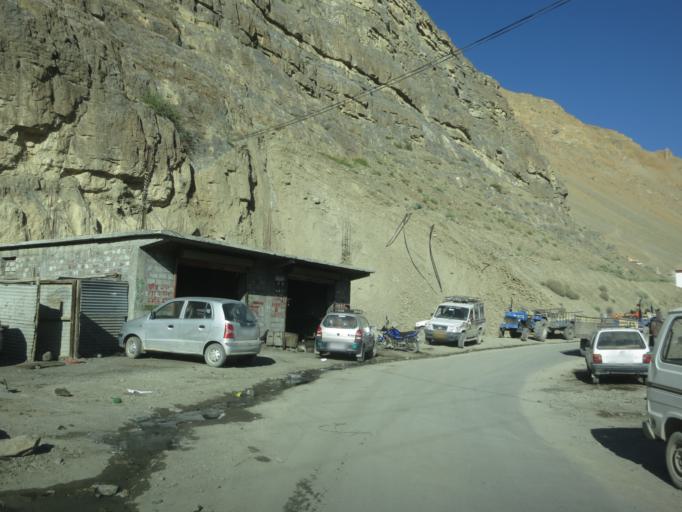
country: IN
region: Himachal Pradesh
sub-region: Shimla
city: Sarahan
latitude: 32.2297
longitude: 78.0678
